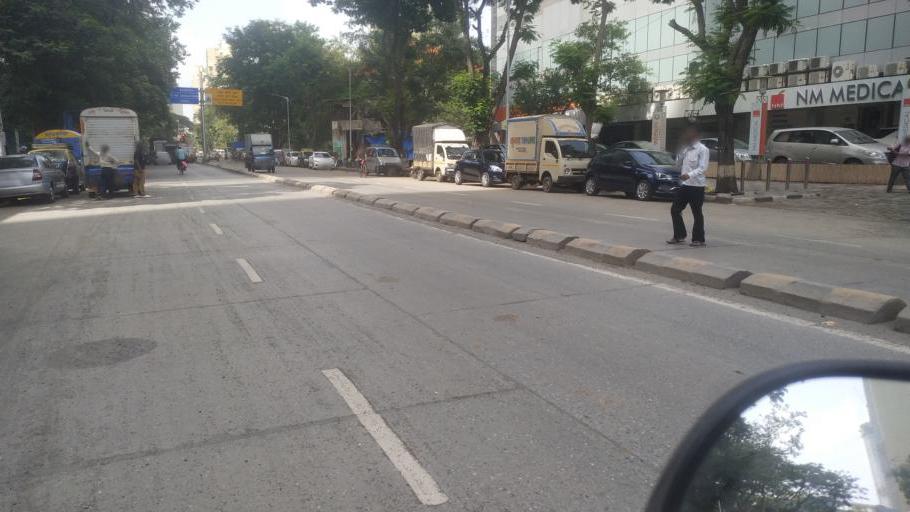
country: IN
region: Maharashtra
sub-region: Mumbai Suburban
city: Mumbai
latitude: 19.0099
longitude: 72.8310
